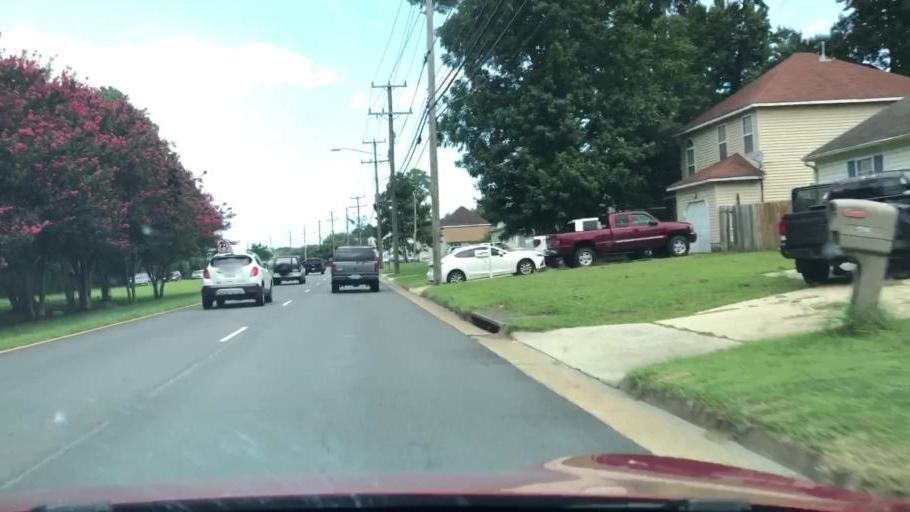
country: US
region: Virginia
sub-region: City of Norfolk
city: Norfolk
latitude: 36.8901
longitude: -76.1382
